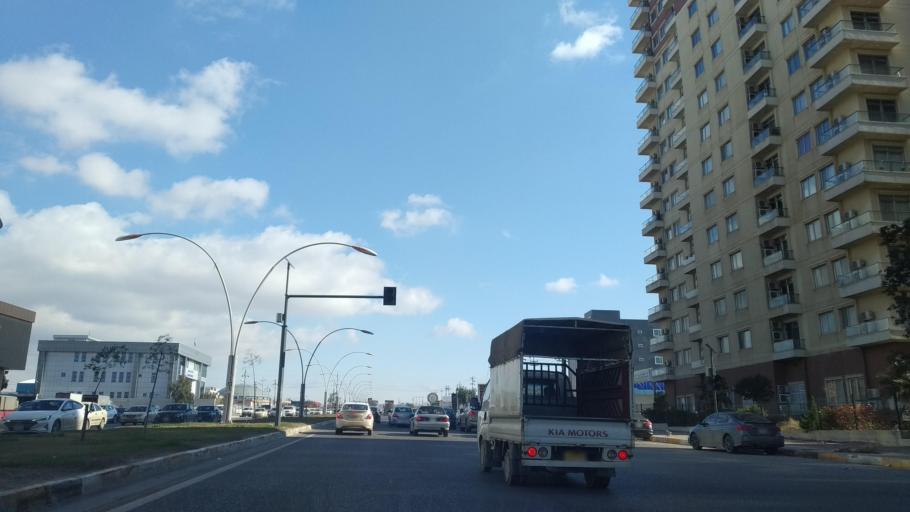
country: IQ
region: Arbil
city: Erbil
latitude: 36.2053
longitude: 44.1215
